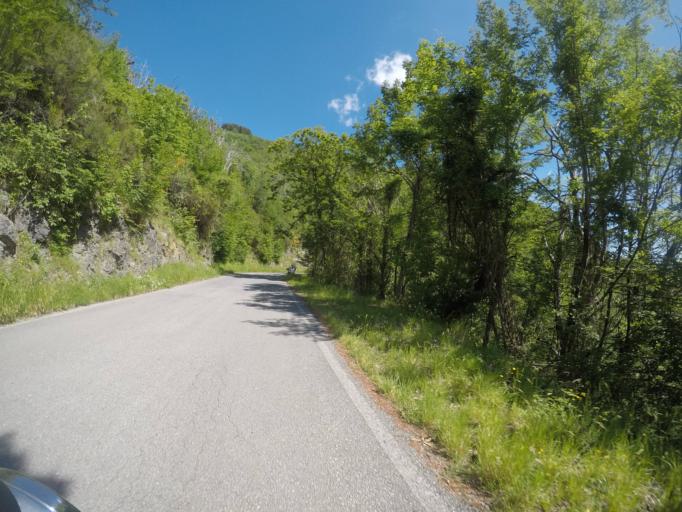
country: IT
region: Tuscany
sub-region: Provincia di Lucca
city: Careggine
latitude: 44.0733
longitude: 10.3309
